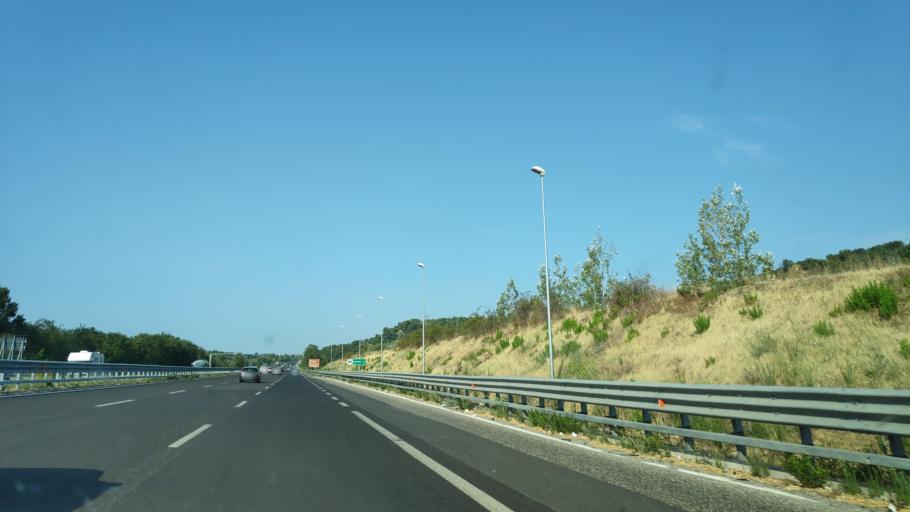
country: IT
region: Campania
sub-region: Provincia di Salerno
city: Serre
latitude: 40.6173
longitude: 15.1640
